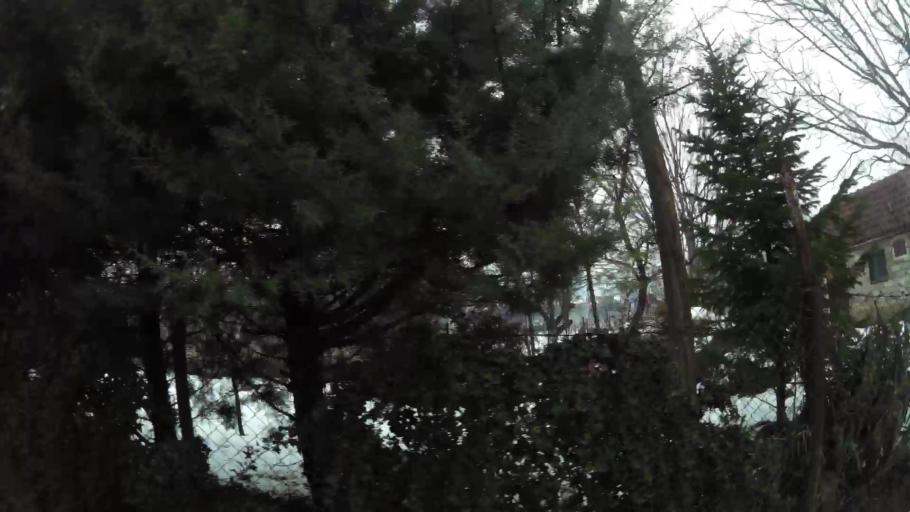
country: MK
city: Kondovo
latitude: 42.0367
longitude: 21.3434
